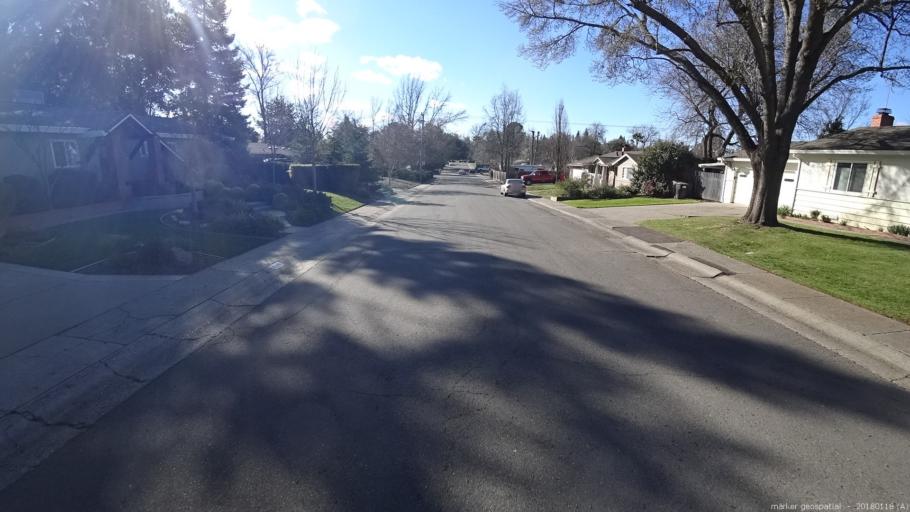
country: US
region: California
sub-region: Sacramento County
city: Orangevale
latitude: 38.6664
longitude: -121.2319
